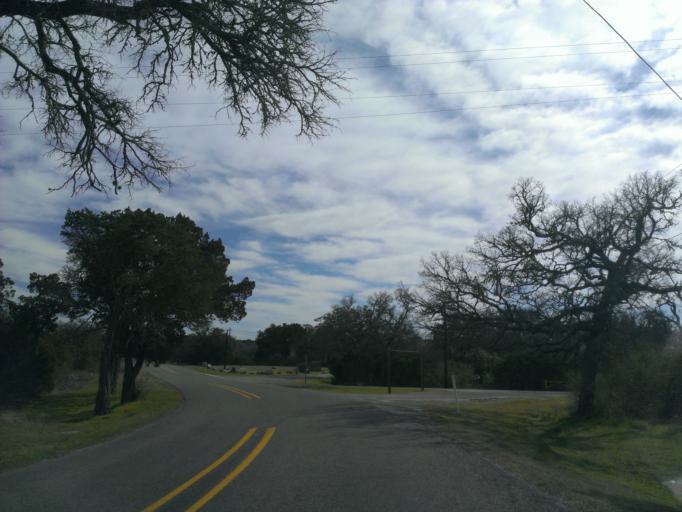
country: US
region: Texas
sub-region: Llano County
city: Kingsland
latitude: 30.6858
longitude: -98.3510
